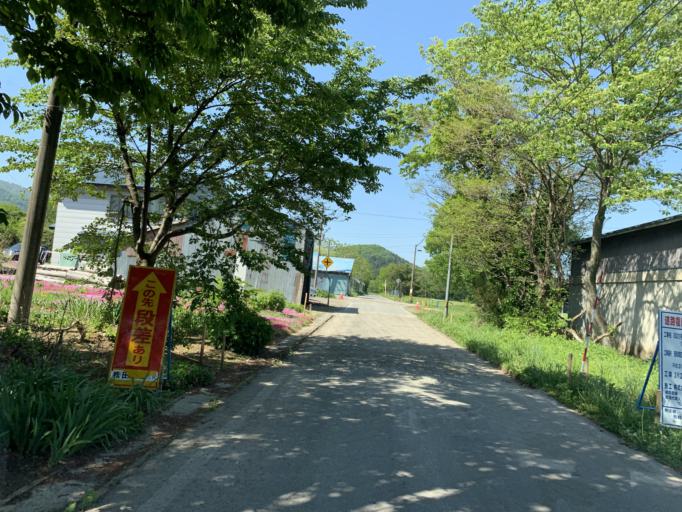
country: JP
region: Iwate
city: Shizukuishi
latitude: 39.5592
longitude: 140.8315
